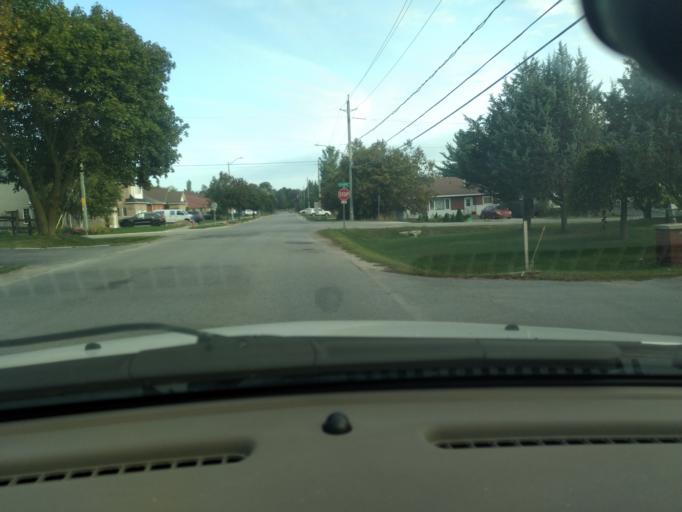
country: CA
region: Ontario
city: Innisfil
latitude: 44.3161
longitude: -79.5528
